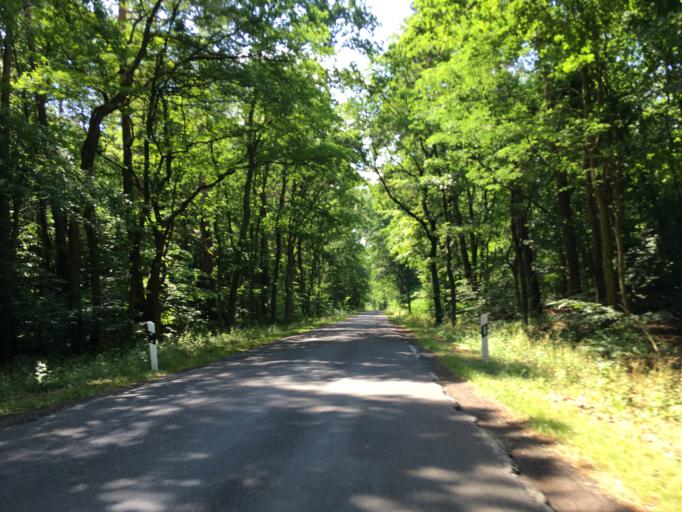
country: DE
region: Brandenburg
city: Hohenfinow
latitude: 52.8003
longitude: 13.9061
